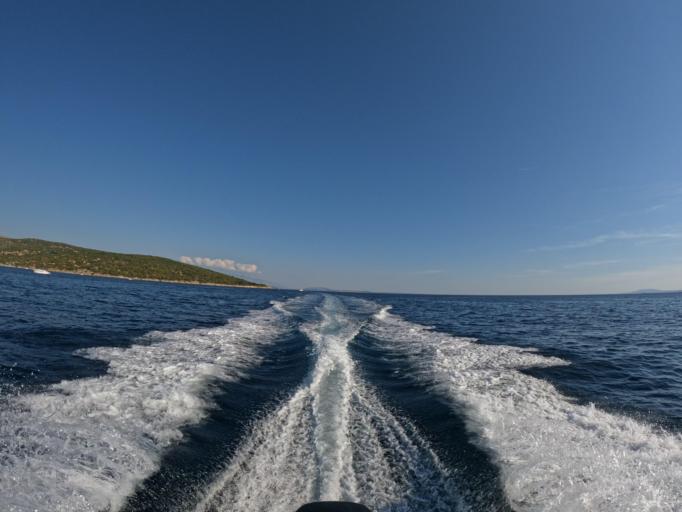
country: HR
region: Primorsko-Goranska
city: Punat
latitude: 44.9874
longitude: 14.6080
